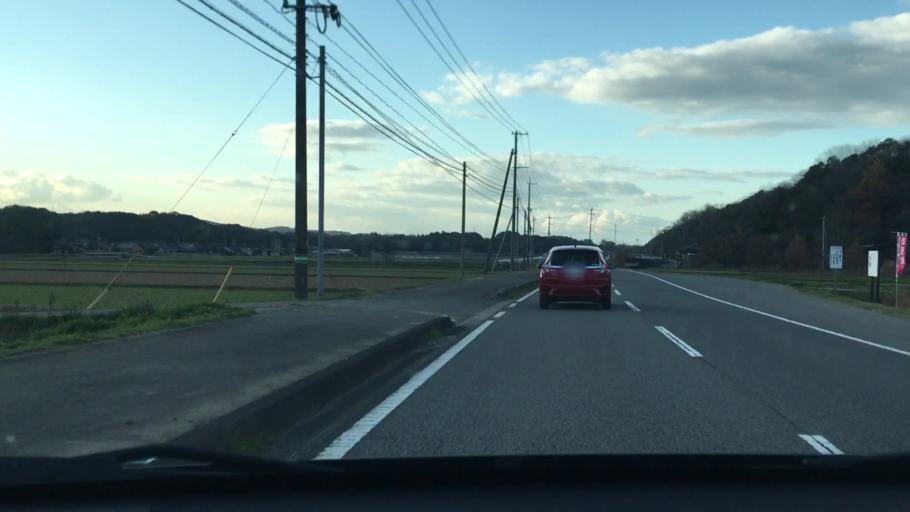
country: JP
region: Oita
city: Bungo-Takada-shi
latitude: 33.5051
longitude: 131.3637
